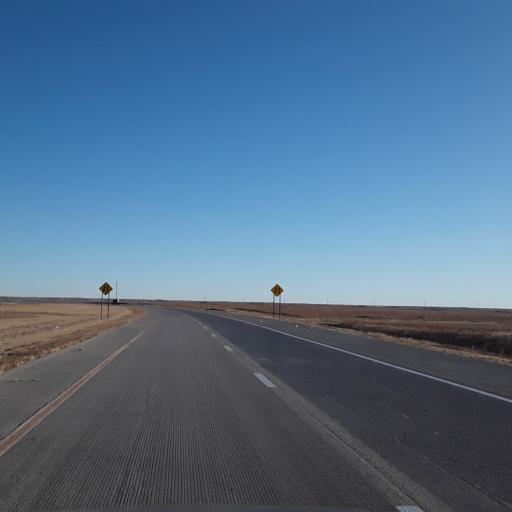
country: US
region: Kansas
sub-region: Seward County
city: Liberal
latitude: 37.1122
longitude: -100.7792
